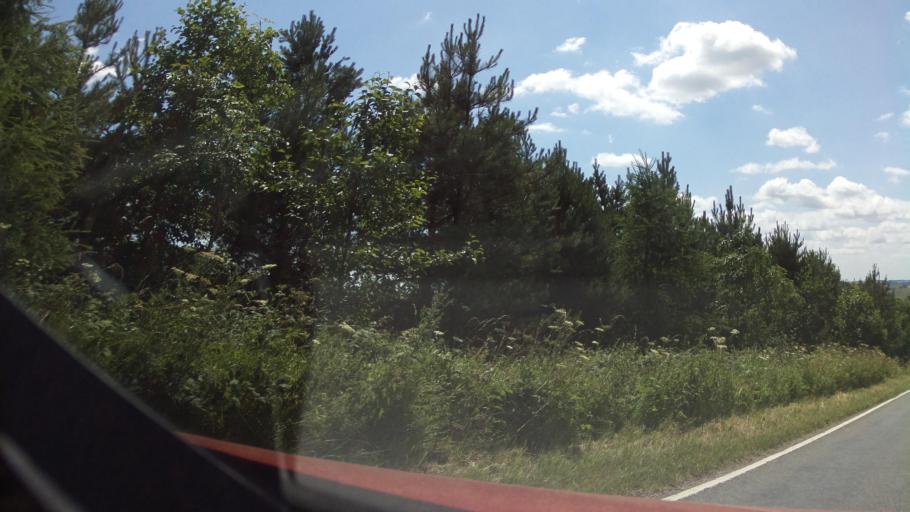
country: GB
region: England
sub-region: Derbyshire
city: Ashbourne
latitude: 53.1082
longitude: -1.7584
